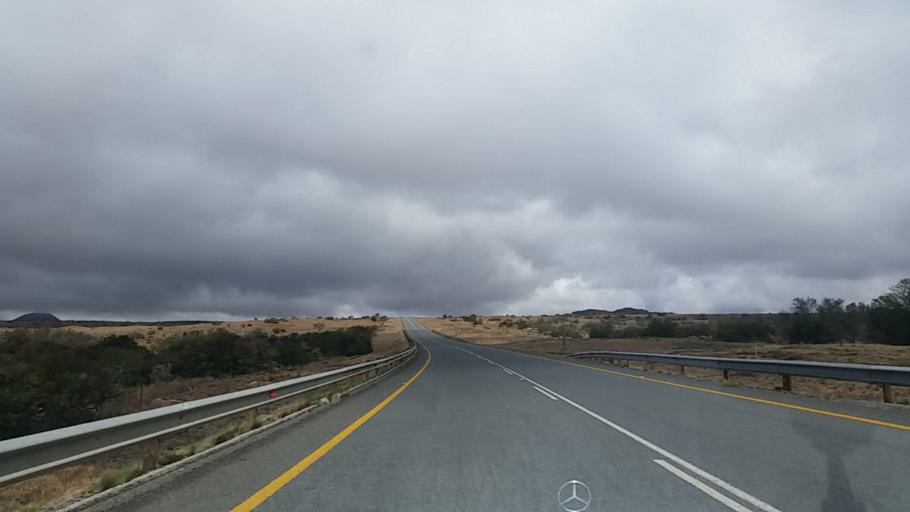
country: ZA
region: Eastern Cape
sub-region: Cacadu District Municipality
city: Graaff-Reinet
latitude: -32.0406
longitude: 24.6191
